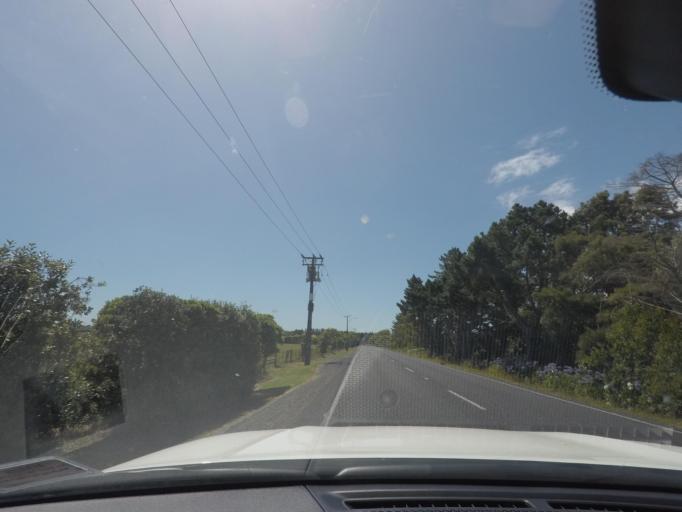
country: NZ
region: Auckland
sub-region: Auckland
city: Parakai
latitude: -36.6711
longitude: 174.4400
